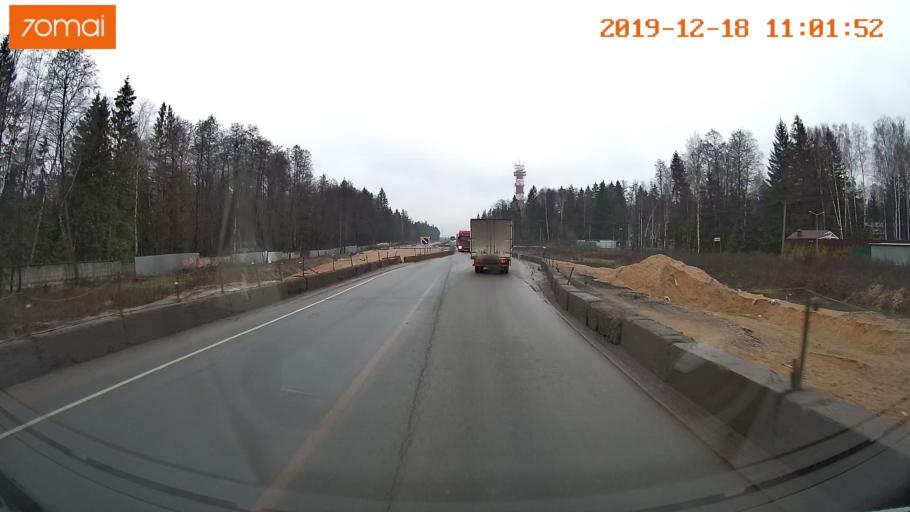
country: RU
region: Moskovskaya
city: Golitsyno
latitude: 55.5732
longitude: 36.9984
